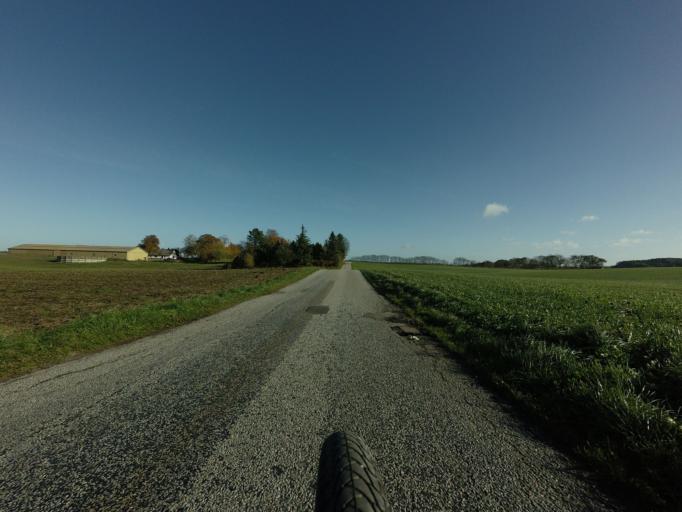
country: DK
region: Central Jutland
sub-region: Syddjurs Kommune
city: Ryomgard
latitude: 56.4570
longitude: 10.6273
